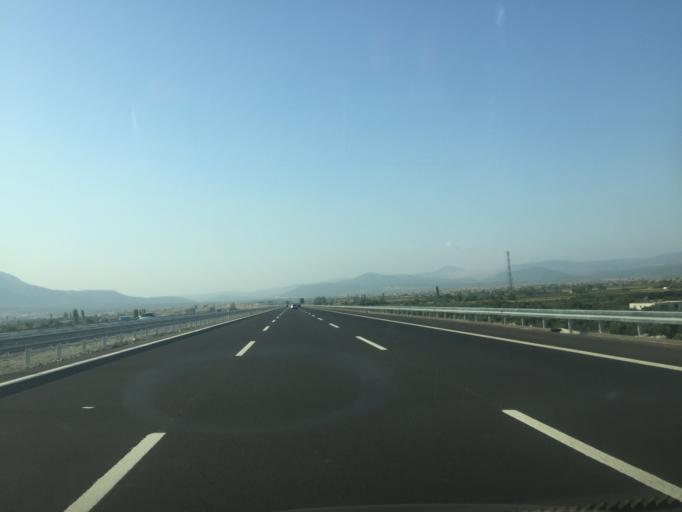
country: TR
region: Manisa
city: Kirkagac
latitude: 39.0760
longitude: 27.7159
